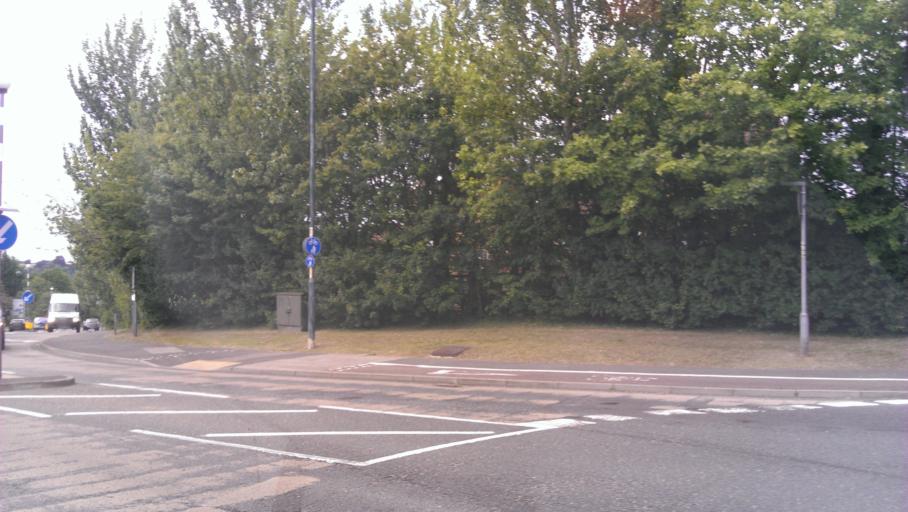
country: GB
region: England
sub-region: Kent
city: Strood
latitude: 51.4089
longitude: 0.4988
